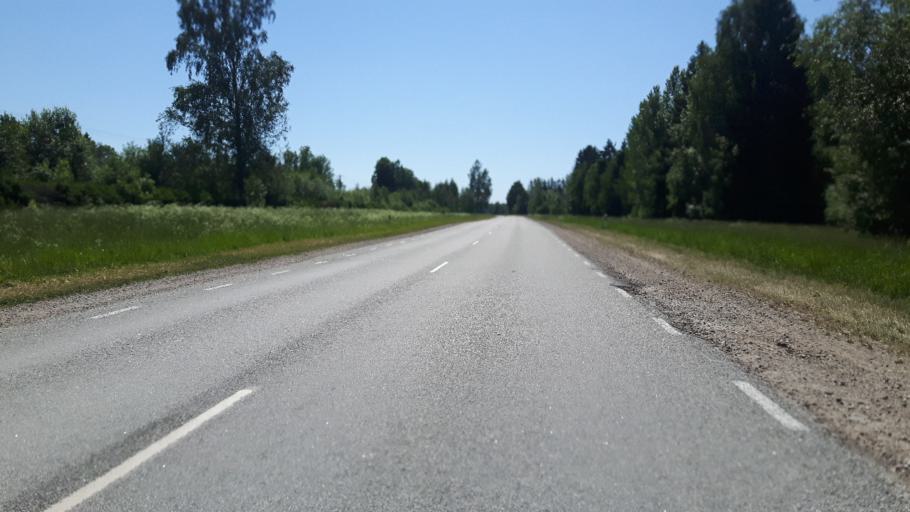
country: EE
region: Paernumaa
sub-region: Tootsi vald
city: Tootsi
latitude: 58.4650
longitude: 24.7848
